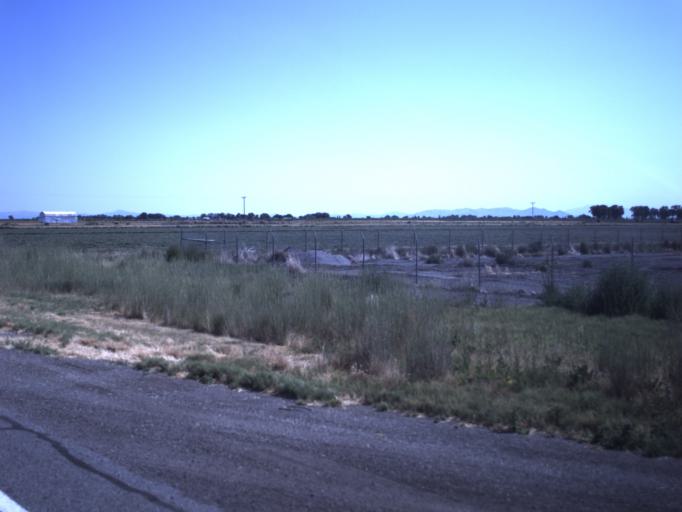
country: US
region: Utah
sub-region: Millard County
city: Delta
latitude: 39.3286
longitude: -112.6523
